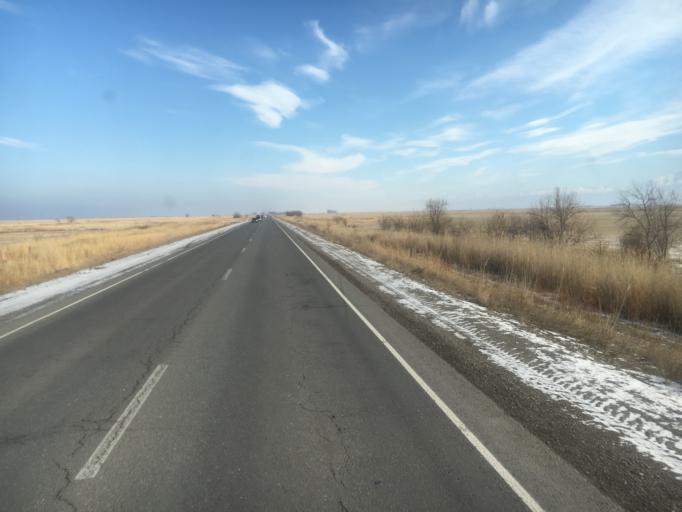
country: KG
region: Chuy
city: Tokmok
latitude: 43.3548
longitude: 75.4360
